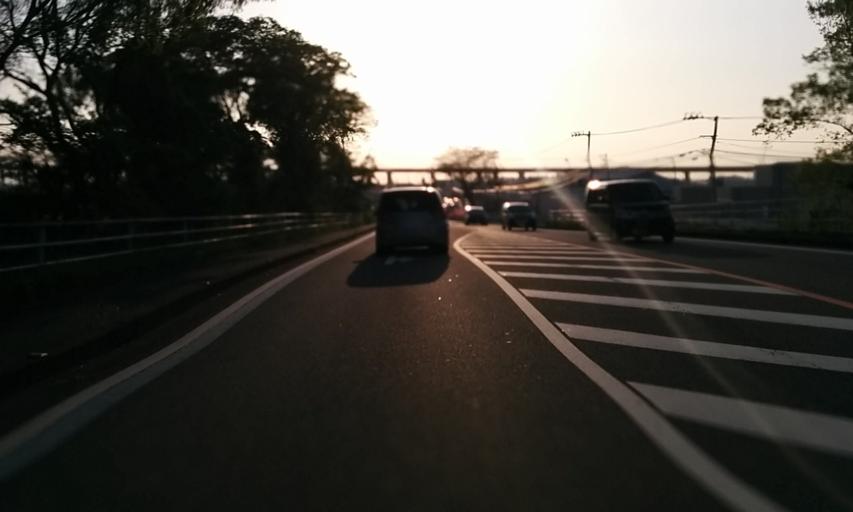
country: JP
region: Ehime
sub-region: Shikoku-chuo Shi
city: Matsuyama
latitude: 33.7891
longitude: 132.7782
